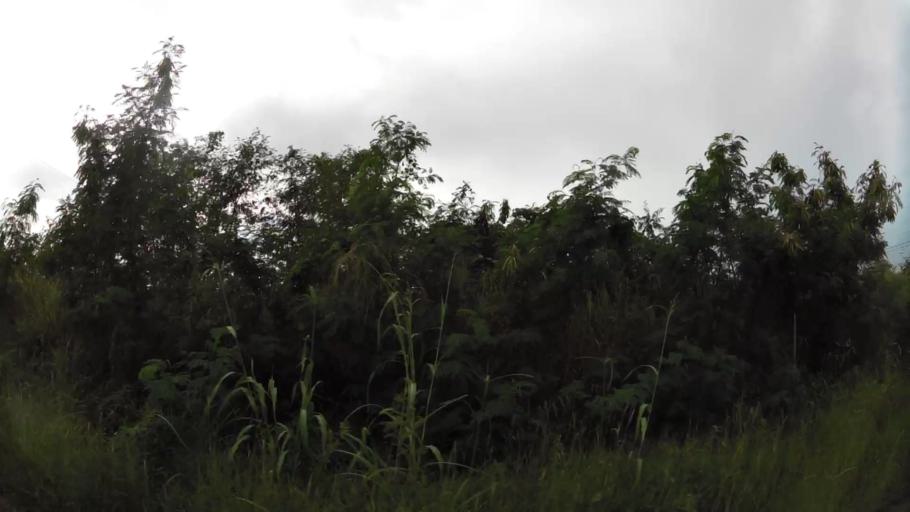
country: AG
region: Saint John
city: Potters Village
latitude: 17.0965
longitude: -61.8131
